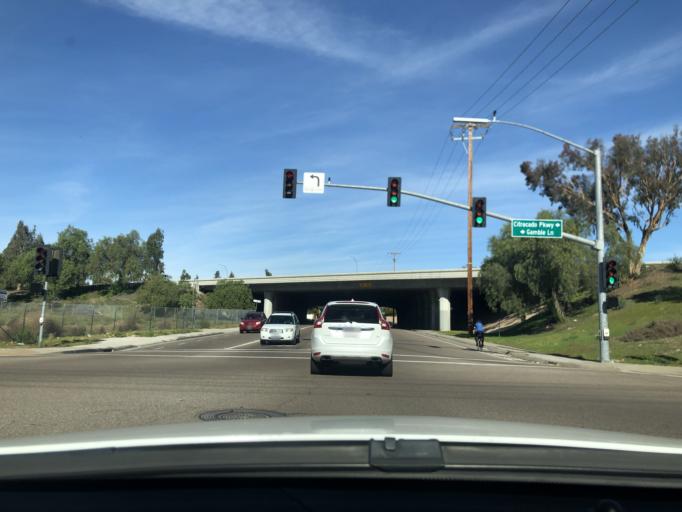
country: US
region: California
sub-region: San Diego County
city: Escondido
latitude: 33.0927
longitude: -117.0843
